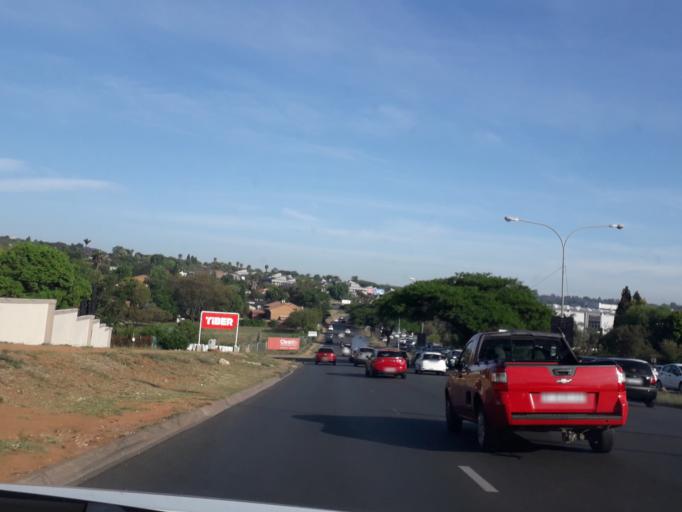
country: ZA
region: Gauteng
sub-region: City of Johannesburg Metropolitan Municipality
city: Johannesburg
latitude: -26.0930
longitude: 28.0290
